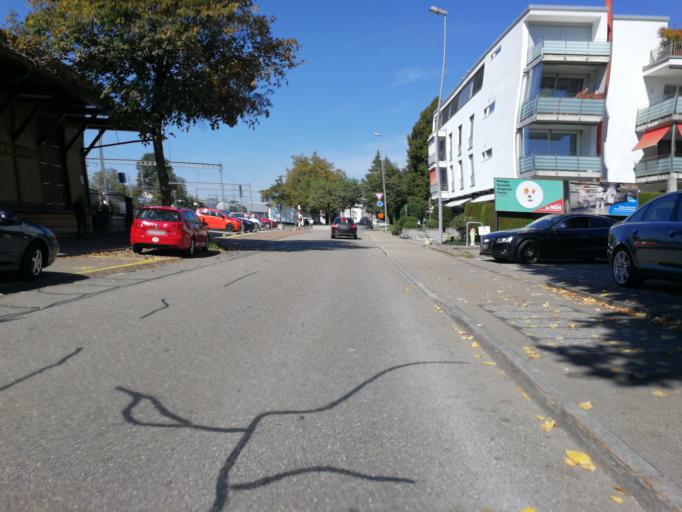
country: CH
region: Zurich
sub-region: Bezirk Hinwil
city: Hinwil
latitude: 47.3002
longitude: 8.8400
